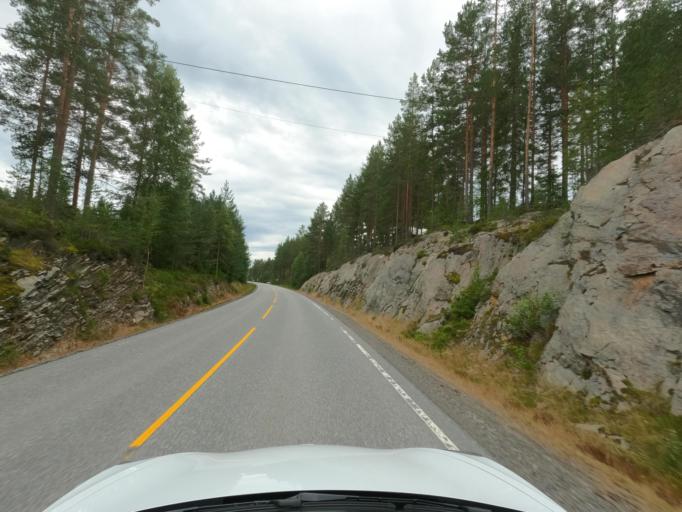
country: NO
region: Telemark
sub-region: Hjartdal
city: Sauland
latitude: 59.7259
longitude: 9.0183
